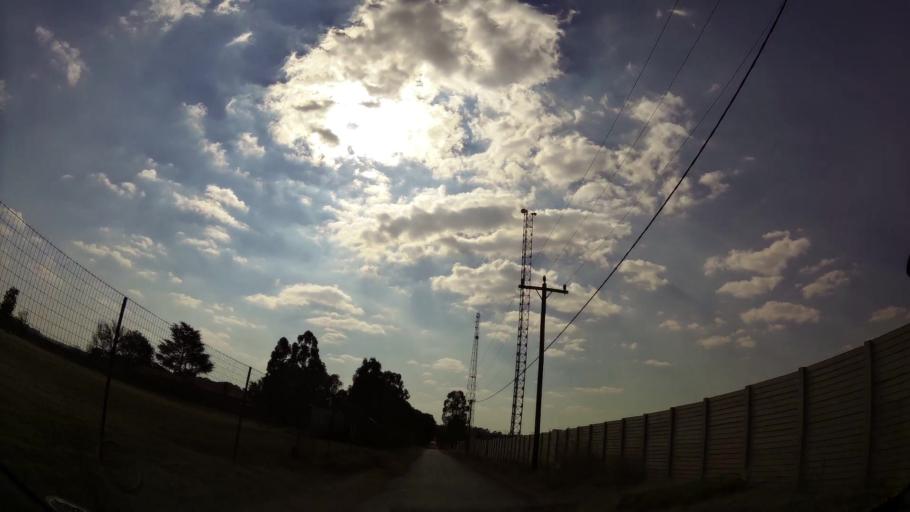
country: ZA
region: Gauteng
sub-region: Ekurhuleni Metropolitan Municipality
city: Benoni
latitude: -26.0886
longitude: 28.3651
